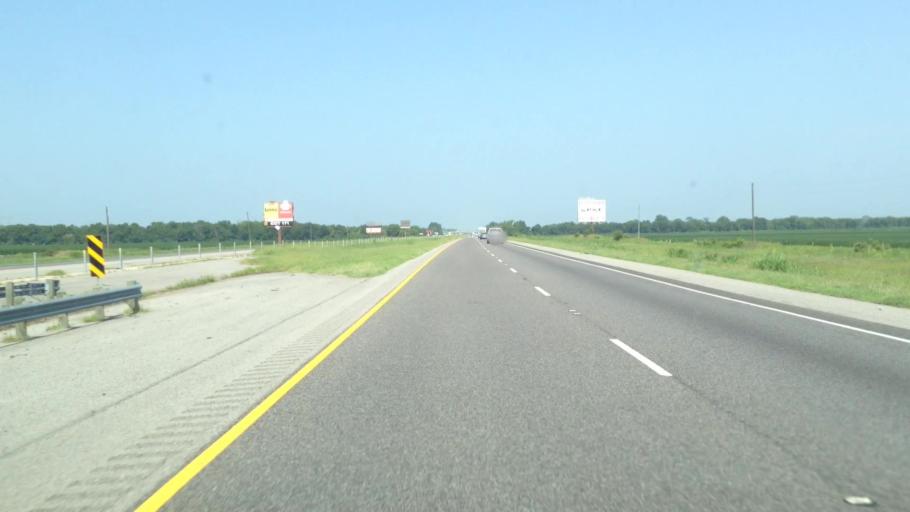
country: US
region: Mississippi
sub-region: Warren County
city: Vicksburg
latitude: 32.3261
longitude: -91.0005
